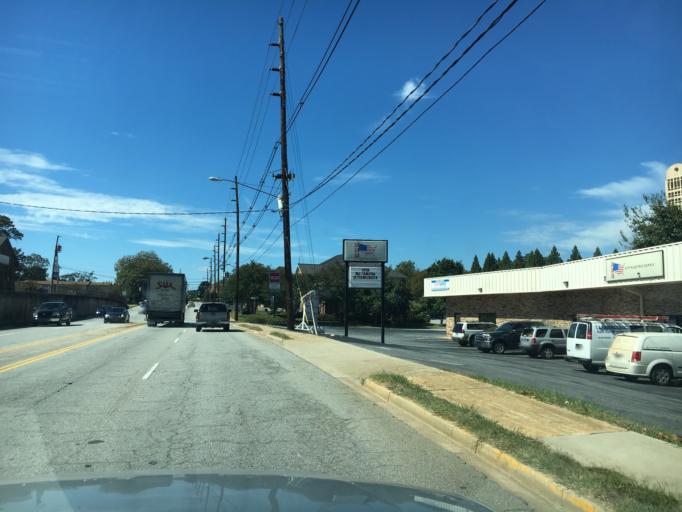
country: US
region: South Carolina
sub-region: Spartanburg County
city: Spartanburg
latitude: 34.9476
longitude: -81.9248
